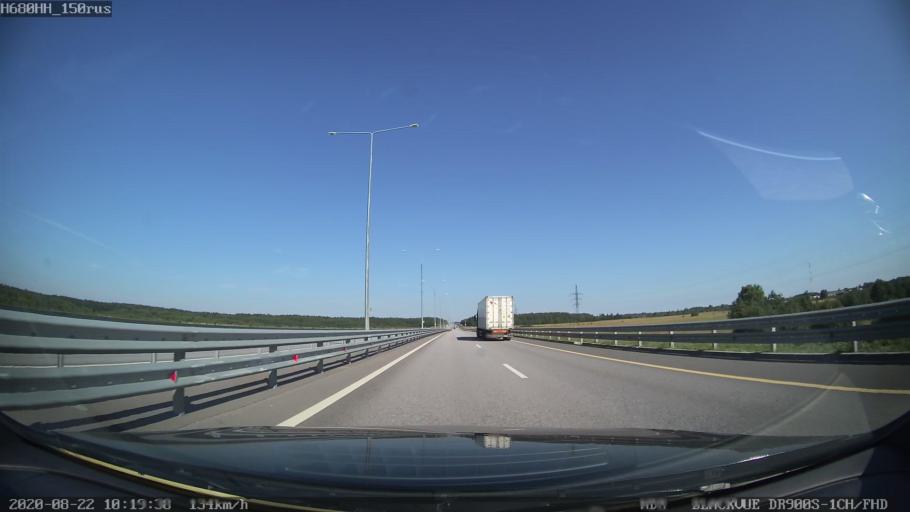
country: RU
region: Tverskaya
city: Zavidovo
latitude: 56.5236
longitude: 36.5006
